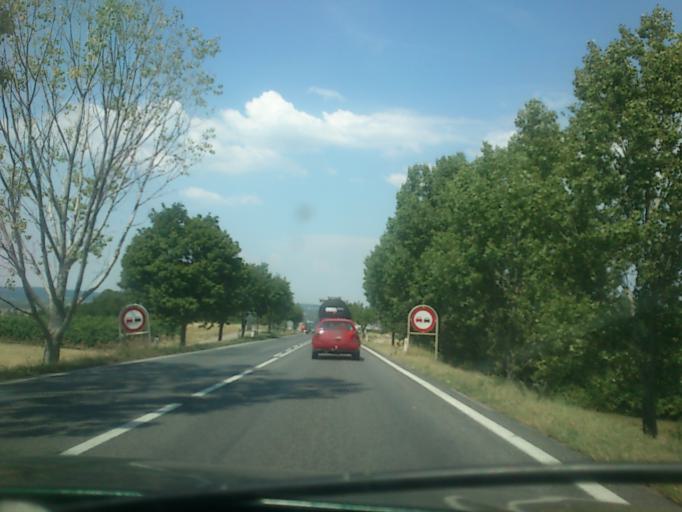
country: AT
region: Lower Austria
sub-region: Politischer Bezirk Mistelbach
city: Poysdorf
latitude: 48.6400
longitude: 16.6390
